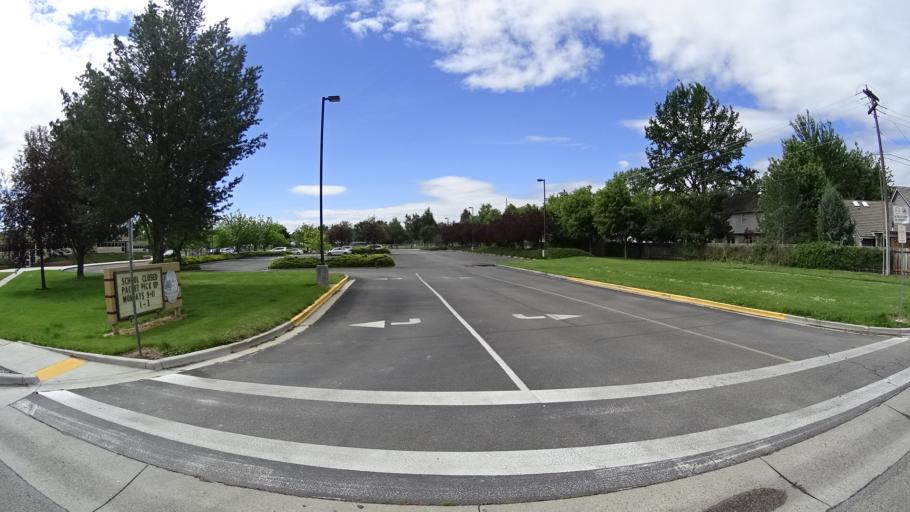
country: US
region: Idaho
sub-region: Ada County
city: Boise
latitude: 43.5788
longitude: -116.1794
